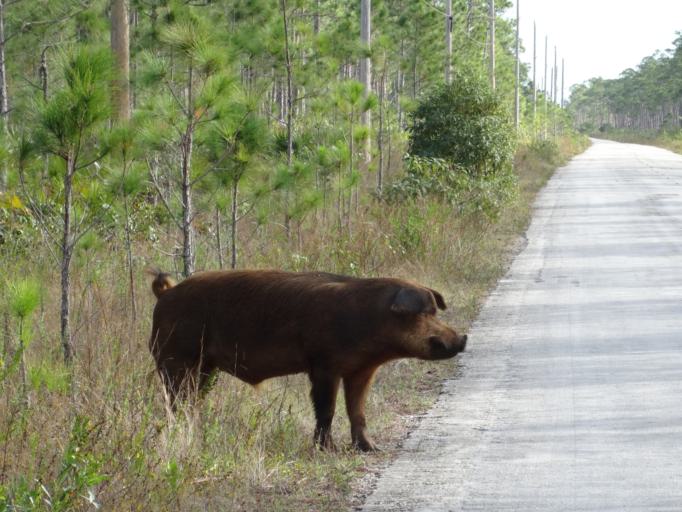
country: BS
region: East Grand Bahama
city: High Rock
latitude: 26.6303
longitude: -78.2245
